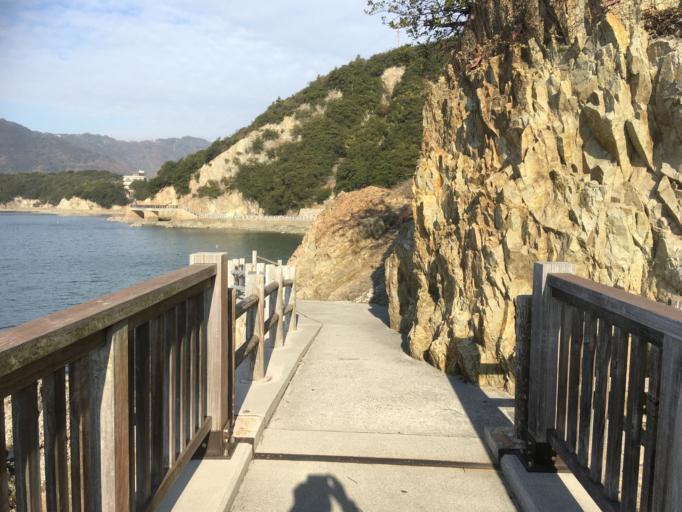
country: JP
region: Hiroshima
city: Fukuyama
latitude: 34.3811
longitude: 133.3940
